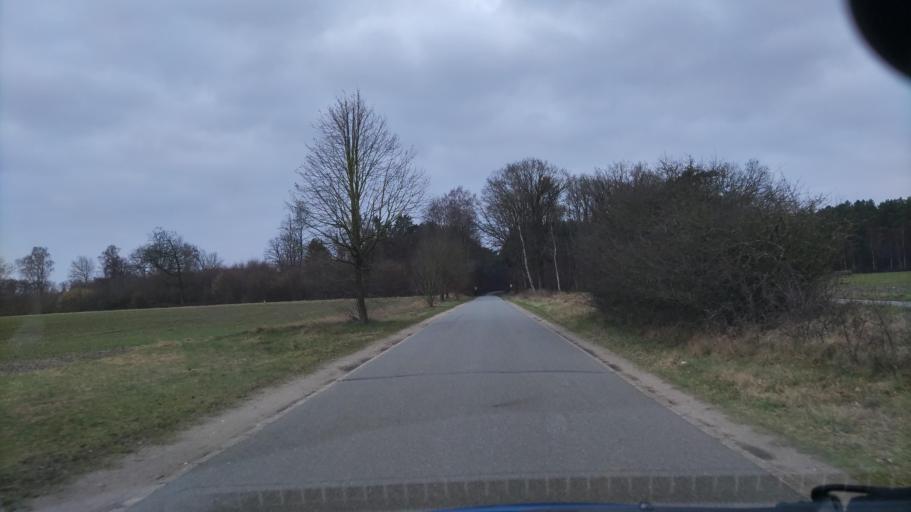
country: DE
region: Lower Saxony
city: Sudergellersen
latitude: 53.2138
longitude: 10.3283
